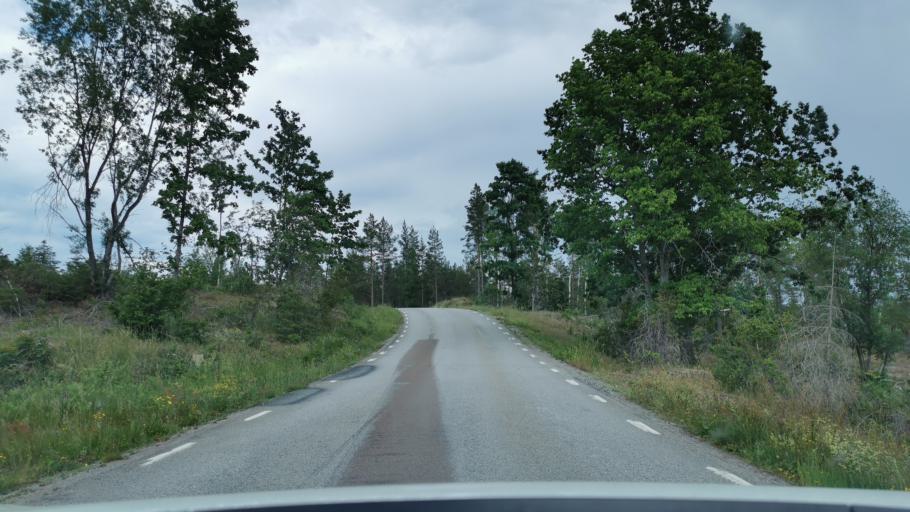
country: SE
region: Vaestra Goetaland
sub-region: Bengtsfors Kommun
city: Dals Langed
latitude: 58.8759
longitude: 12.4042
